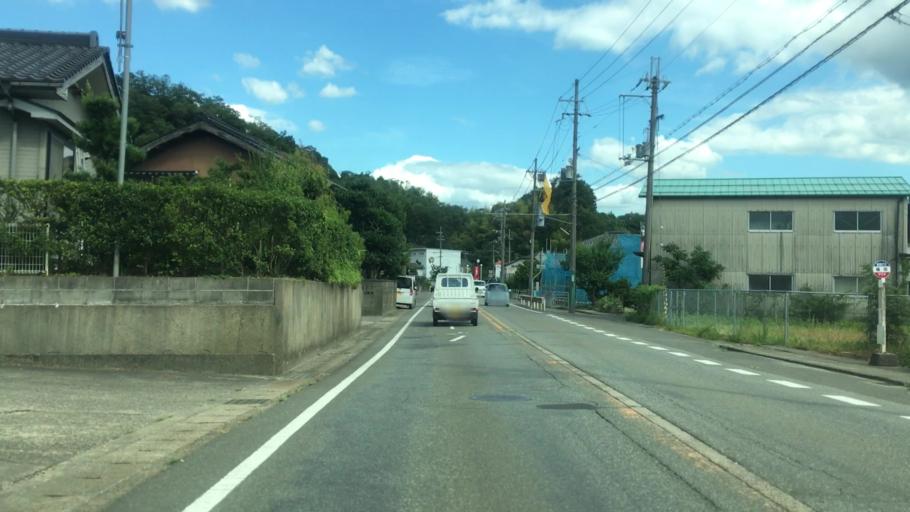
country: JP
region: Hyogo
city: Toyooka
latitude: 35.5546
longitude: 134.7987
